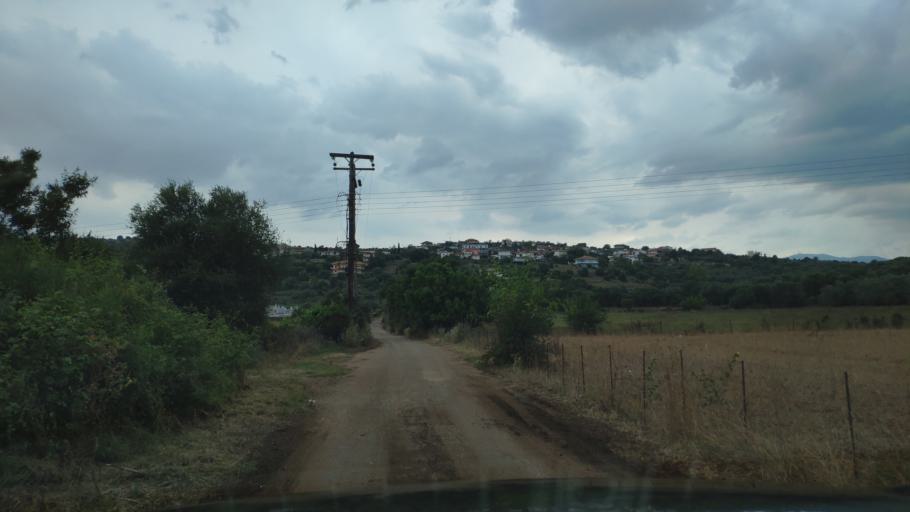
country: GR
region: West Greece
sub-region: Nomos Aitolias kai Akarnanias
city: Amfilochia
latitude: 38.9077
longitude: 21.1096
